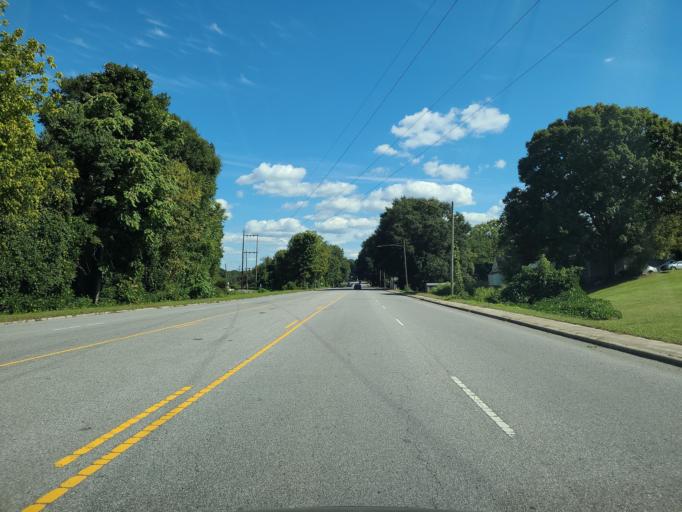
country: US
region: North Carolina
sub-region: Gaston County
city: Gastonia
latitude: 35.2566
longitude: -81.2017
